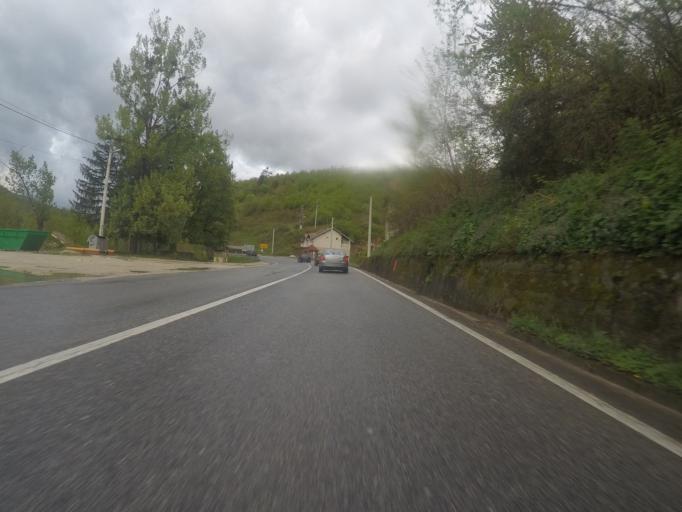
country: BA
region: Federation of Bosnia and Herzegovina
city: Jablanica
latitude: 43.6897
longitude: 17.8317
